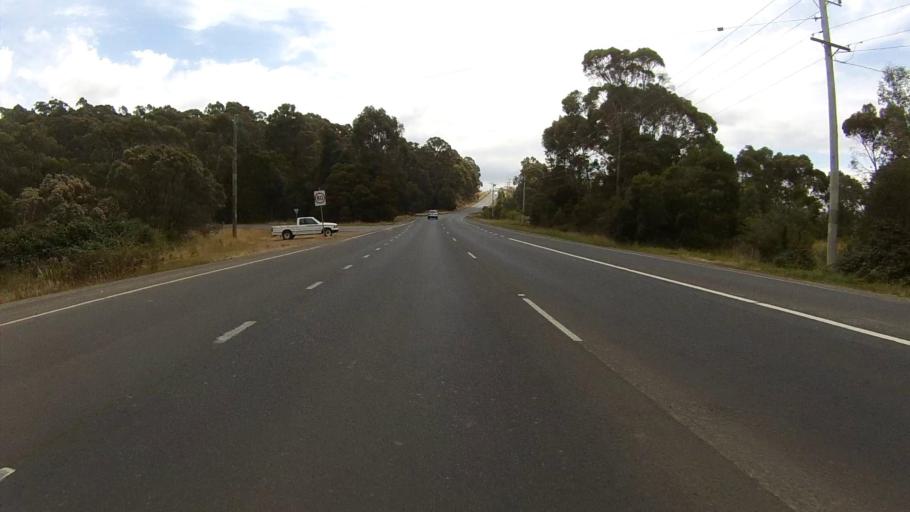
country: AU
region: Tasmania
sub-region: Kingborough
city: Margate
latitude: -43.0743
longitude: 147.2567
